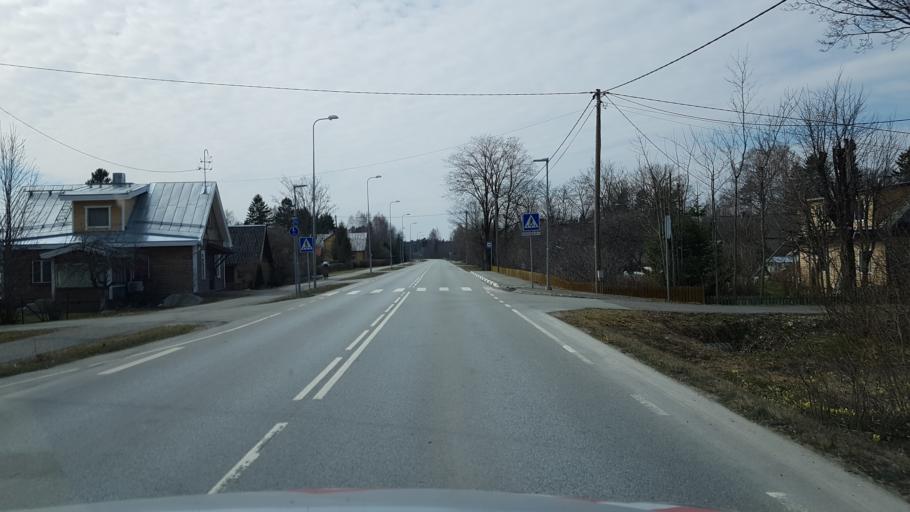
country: EE
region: Ida-Virumaa
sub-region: Aseri vald
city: Aseri
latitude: 59.3518
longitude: 26.8352
